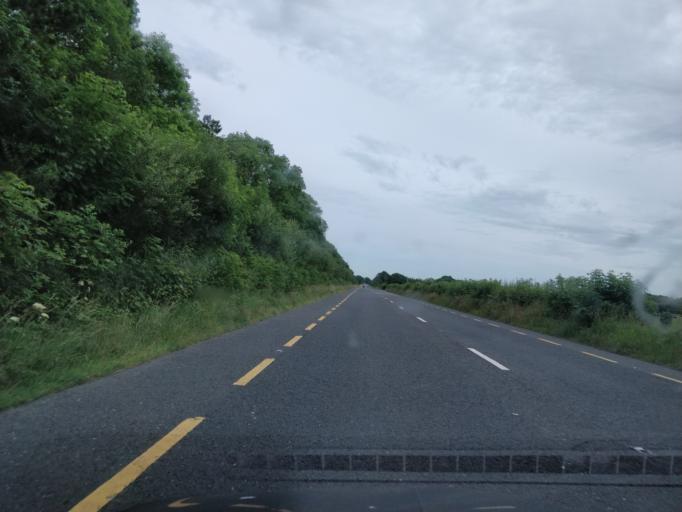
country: IE
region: Leinster
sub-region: Uibh Fhaili
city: Ferbane
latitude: 53.1635
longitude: -7.7973
